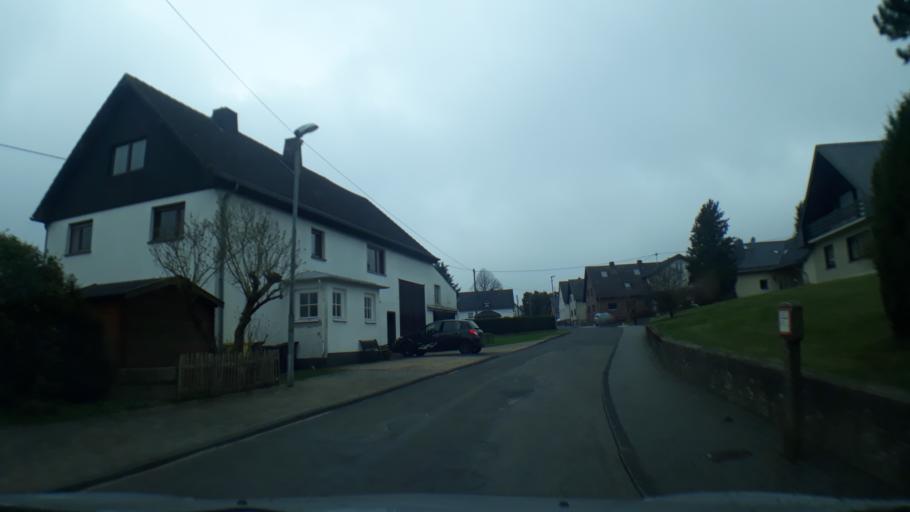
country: DE
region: North Rhine-Westphalia
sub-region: Regierungsbezirk Koln
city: Schleiden
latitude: 50.4942
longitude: 6.5224
